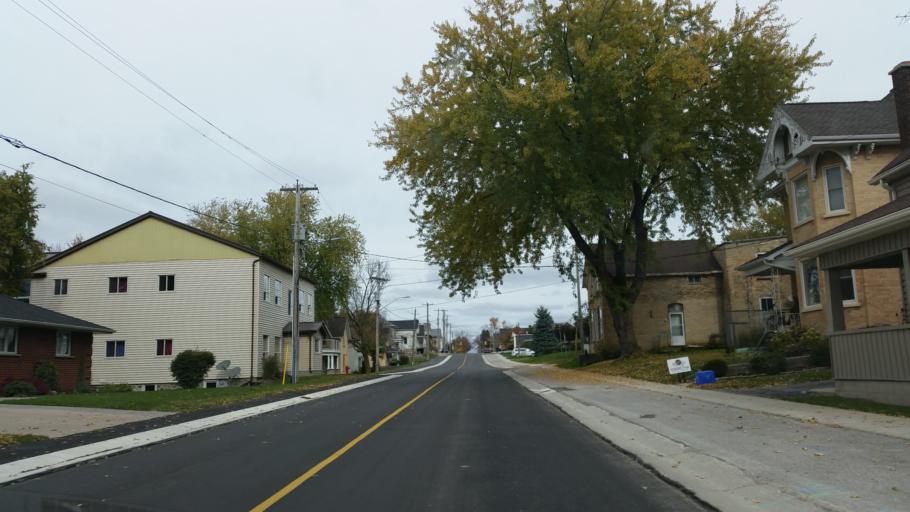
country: CA
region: Ontario
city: Hanover
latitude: 44.0402
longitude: -81.1211
